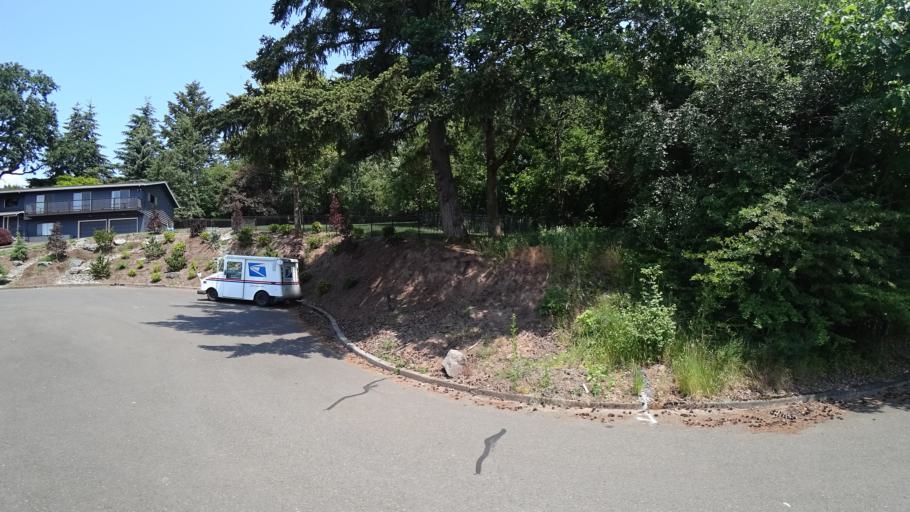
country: US
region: Oregon
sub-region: Clackamas County
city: Happy Valley
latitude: 45.4498
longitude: -122.5541
